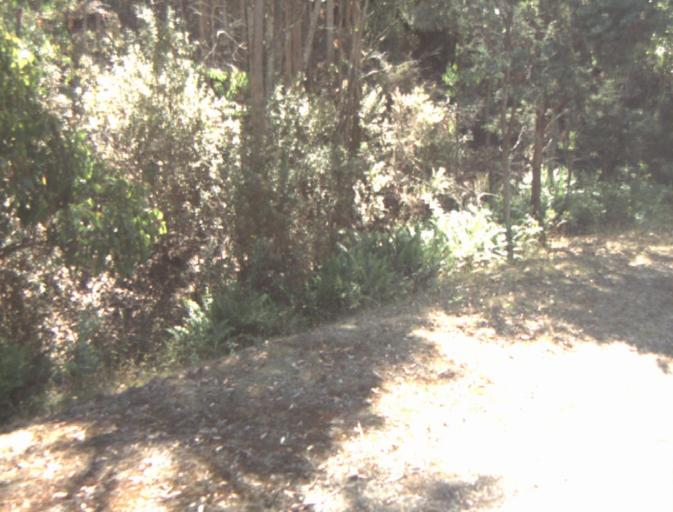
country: AU
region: Tasmania
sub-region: Dorset
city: Scottsdale
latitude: -41.3132
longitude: 147.4012
